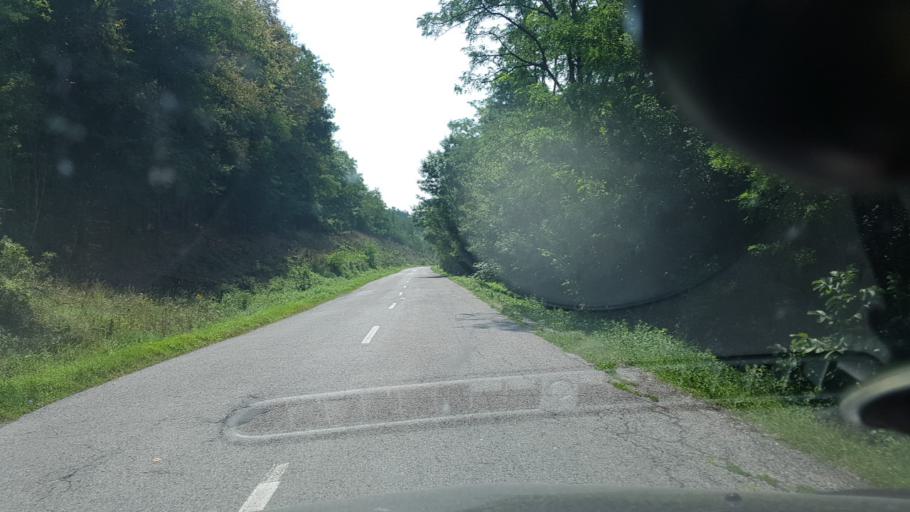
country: SK
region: Banskobystricky
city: Detva
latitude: 48.3936
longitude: 19.3769
